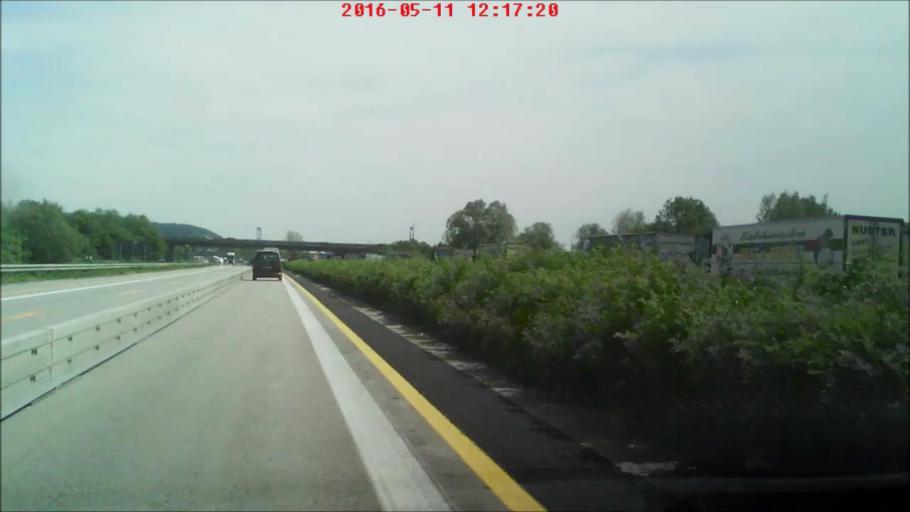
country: DE
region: Bavaria
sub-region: Lower Bavaria
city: Deggendorf
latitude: 48.8200
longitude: 12.9353
